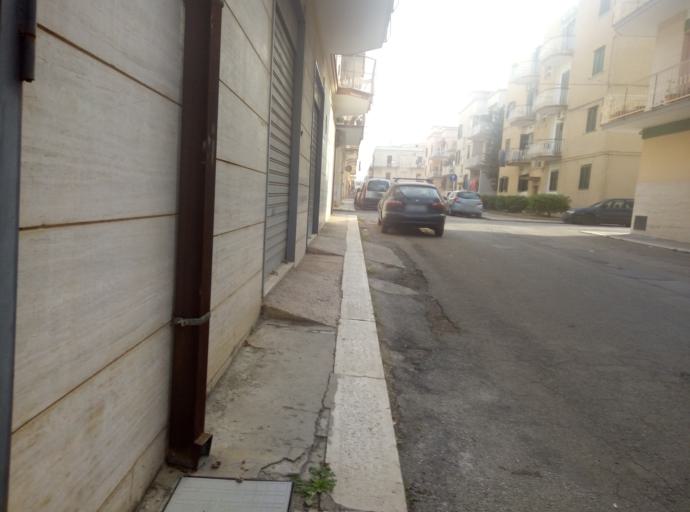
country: IT
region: Apulia
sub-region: Provincia di Bari
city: Ruvo di Puglia
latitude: 41.1219
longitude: 16.4860
